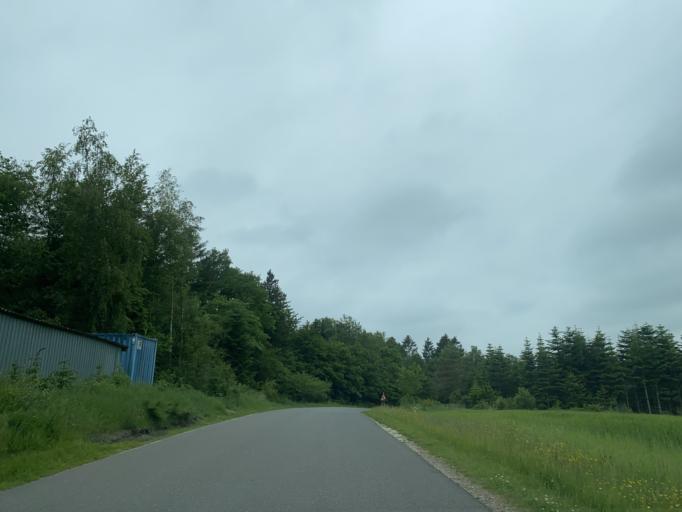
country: DK
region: Central Jutland
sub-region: Viborg Kommune
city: Bjerringbro
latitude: 56.3583
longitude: 9.6375
